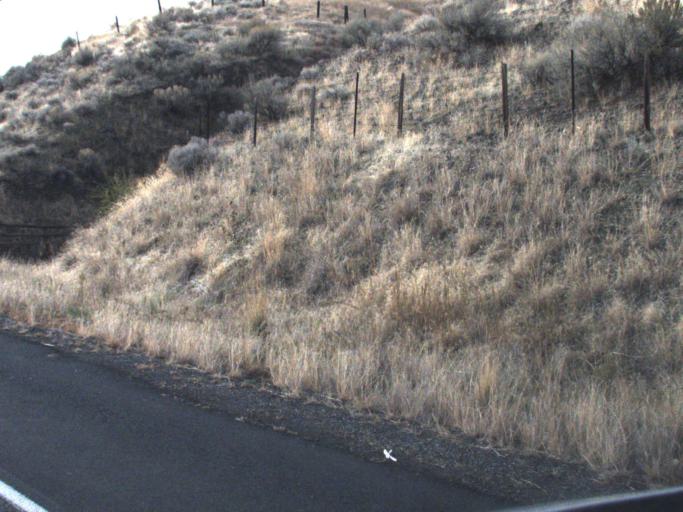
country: US
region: Washington
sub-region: Asotin County
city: Clarkston Heights-Vineland
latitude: 46.4066
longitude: -117.2234
